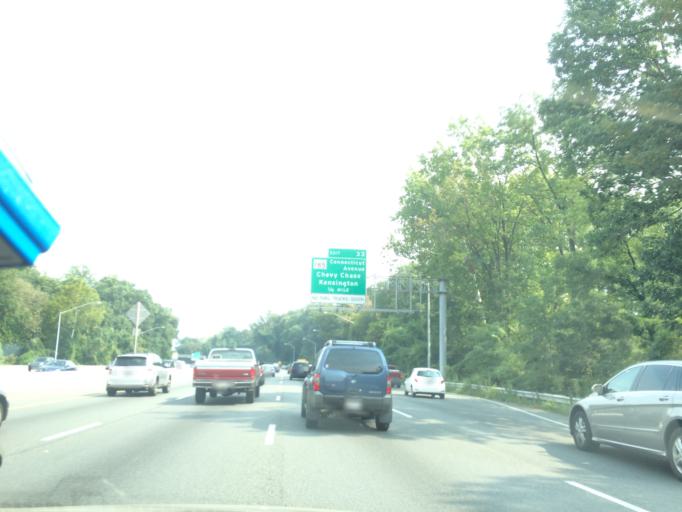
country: US
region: Maryland
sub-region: Montgomery County
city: South Kensington
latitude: 39.0069
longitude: -77.0857
